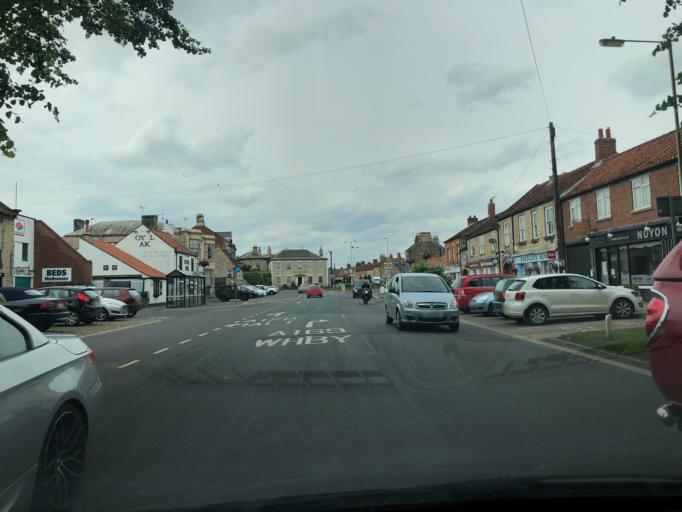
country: GB
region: England
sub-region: North Yorkshire
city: Pickering
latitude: 54.2433
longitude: -0.7737
